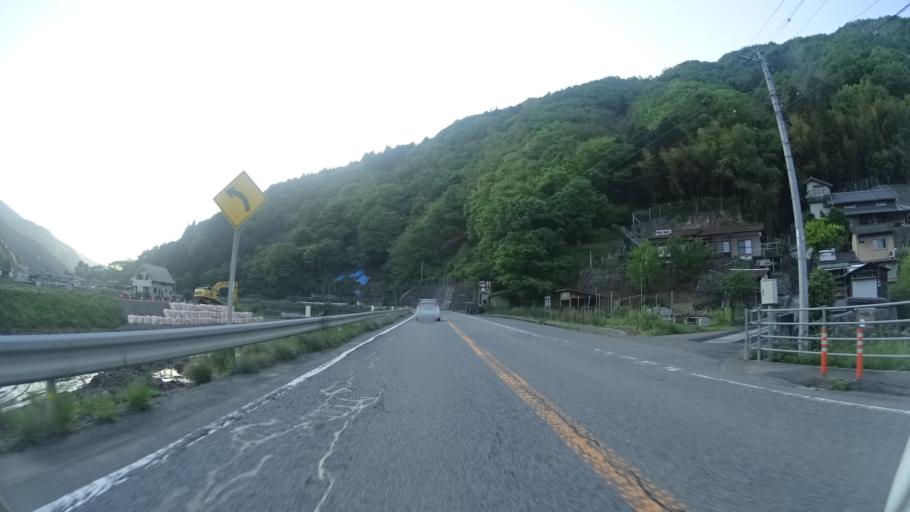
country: JP
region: Tokushima
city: Ikedacho
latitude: 34.0156
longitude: 133.7573
